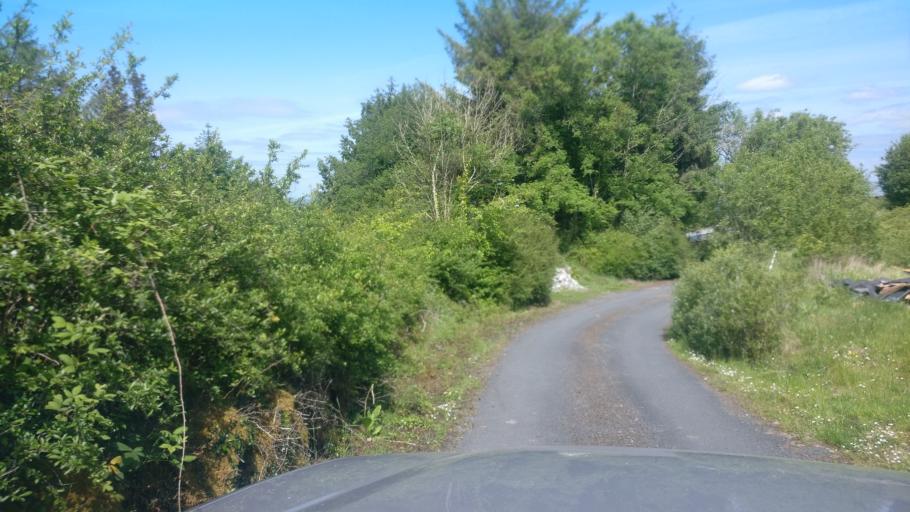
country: IE
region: Connaught
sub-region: County Galway
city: Gort
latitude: 53.1263
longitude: -8.7032
